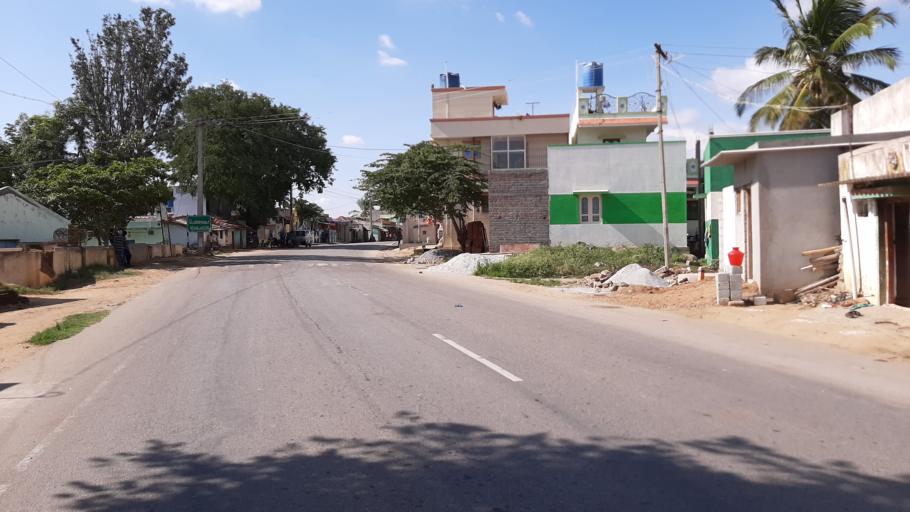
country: IN
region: Tamil Nadu
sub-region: Krishnagiri
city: Denkanikota
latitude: 12.5572
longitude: 77.7847
